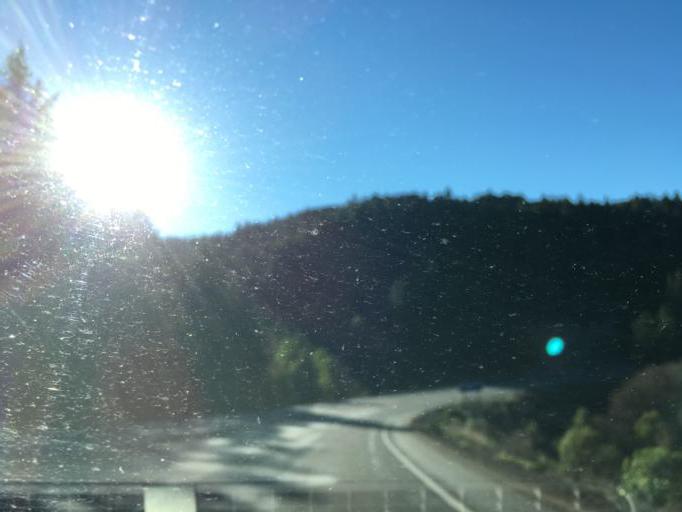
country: US
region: California
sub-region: Mendocino County
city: Laytonville
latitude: 39.8268
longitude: -123.5912
